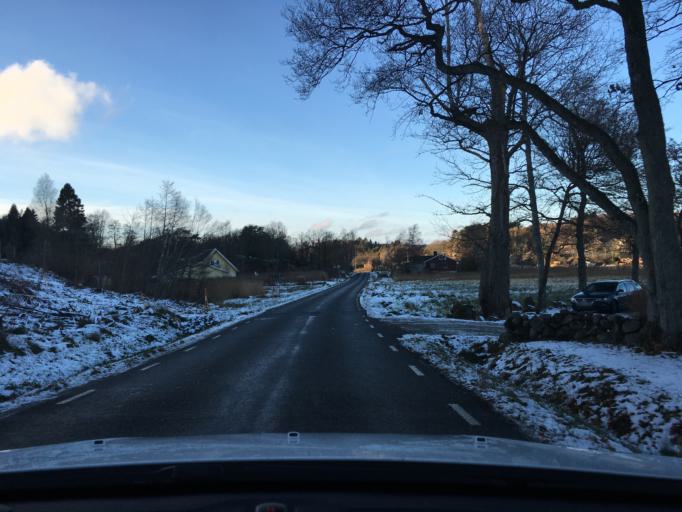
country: SE
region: Vaestra Goetaland
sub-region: Tjorns Kommun
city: Myggenas
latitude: 58.0535
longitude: 11.7008
